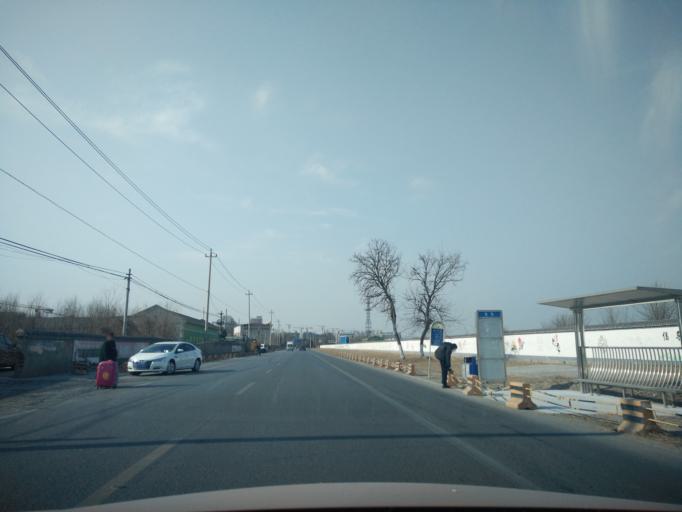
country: CN
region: Beijing
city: Yinghai
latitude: 39.7650
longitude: 116.4560
